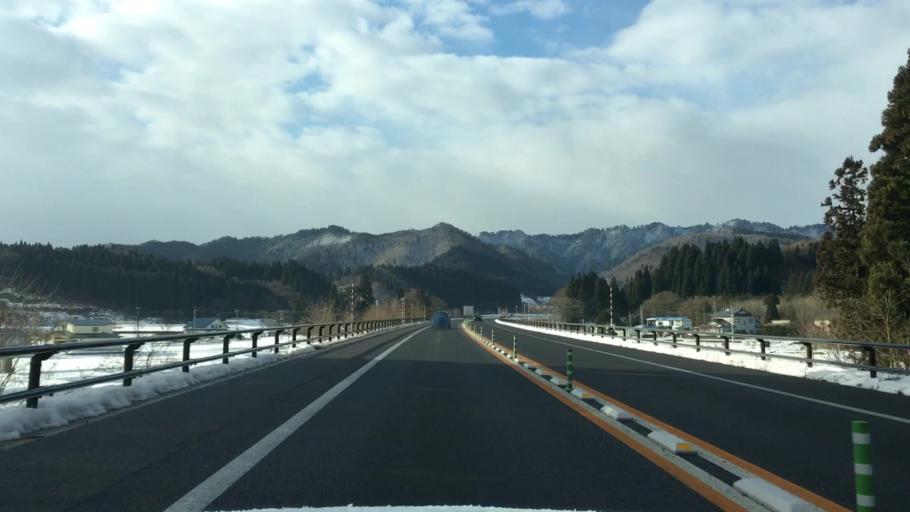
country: JP
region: Akita
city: Odate
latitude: 40.2396
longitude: 140.5049
